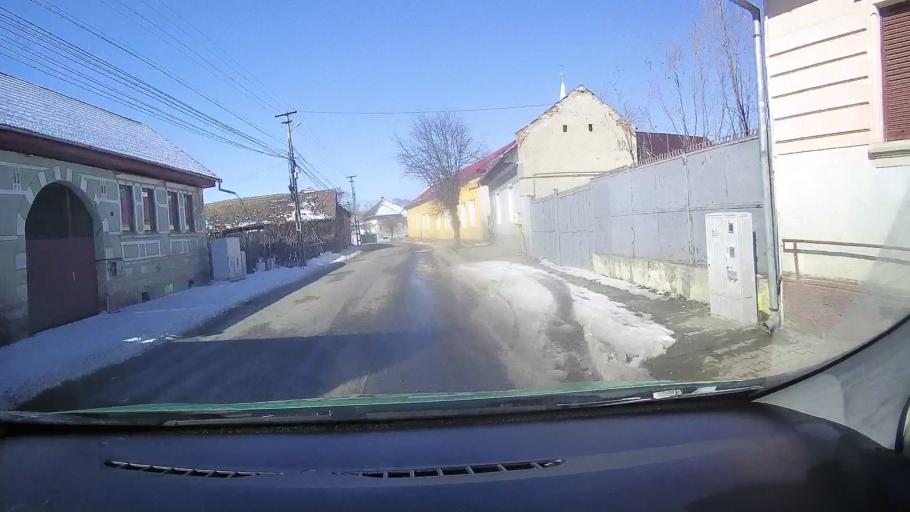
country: RO
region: Brasov
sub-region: Comuna Harseni
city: Harseni
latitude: 45.7884
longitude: 24.9983
